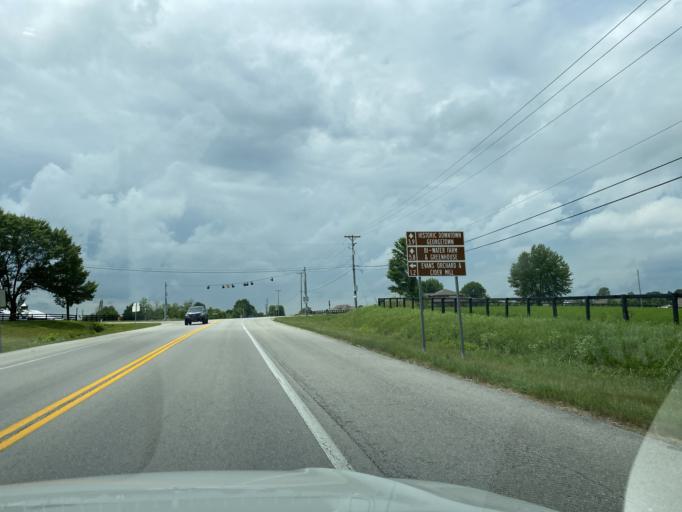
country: US
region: Kentucky
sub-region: Scott County
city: Georgetown
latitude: 38.2194
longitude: -84.4802
